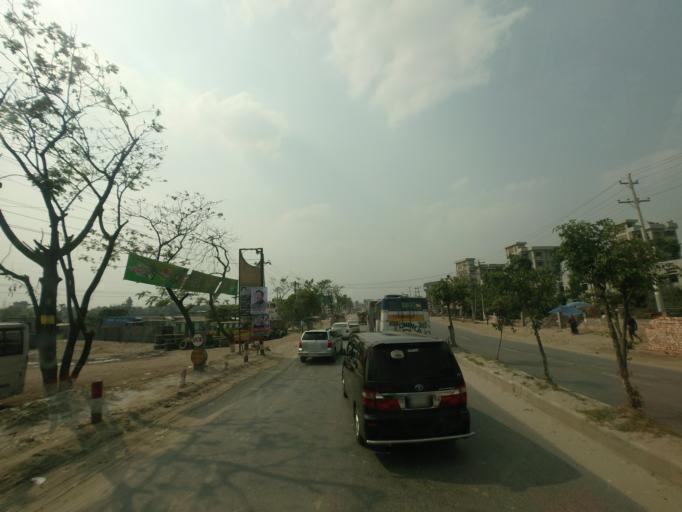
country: BD
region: Dhaka
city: Azimpur
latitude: 23.7872
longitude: 90.3281
